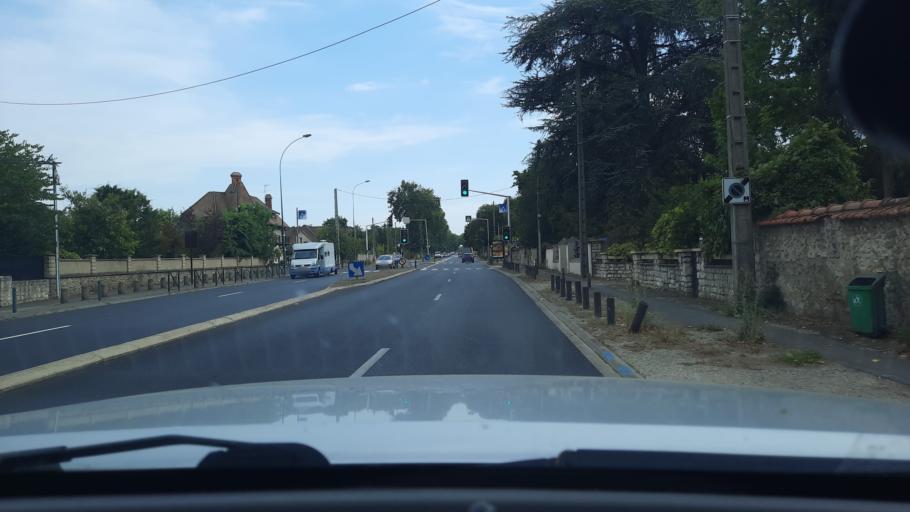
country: FR
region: Ile-de-France
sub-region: Departement de Seine-et-Marne
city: Dammarie-les-Lys
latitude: 48.5219
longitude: 2.6537
